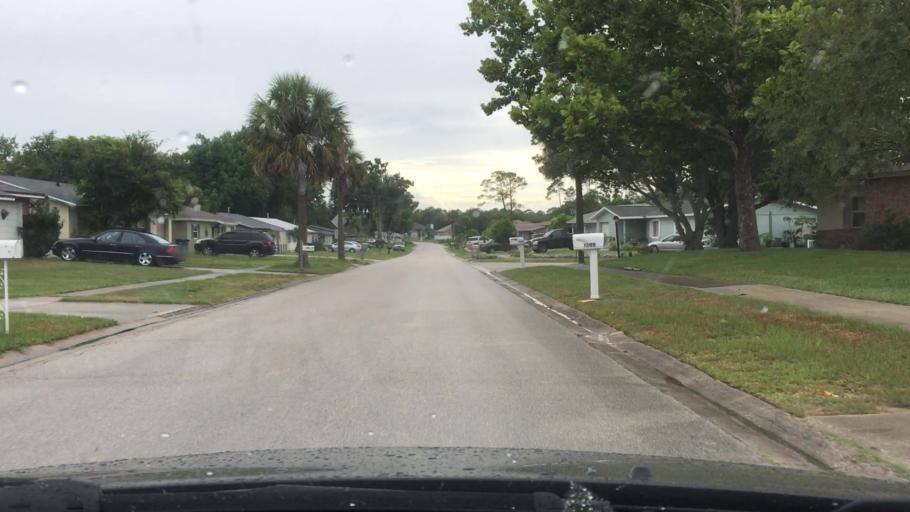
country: US
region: Florida
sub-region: Volusia County
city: Holly Hill
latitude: 29.2515
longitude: -81.0762
